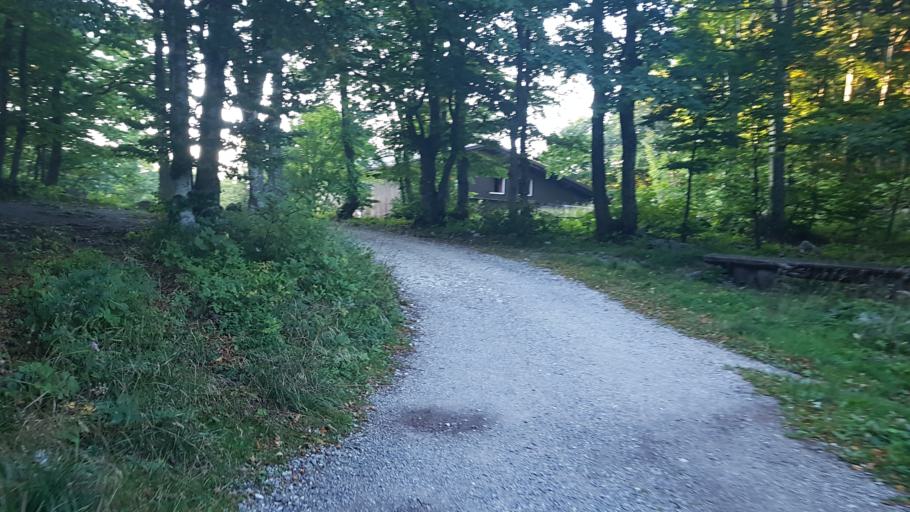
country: SI
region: Vipava
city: Vipava
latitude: 45.7714
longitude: 14.0536
